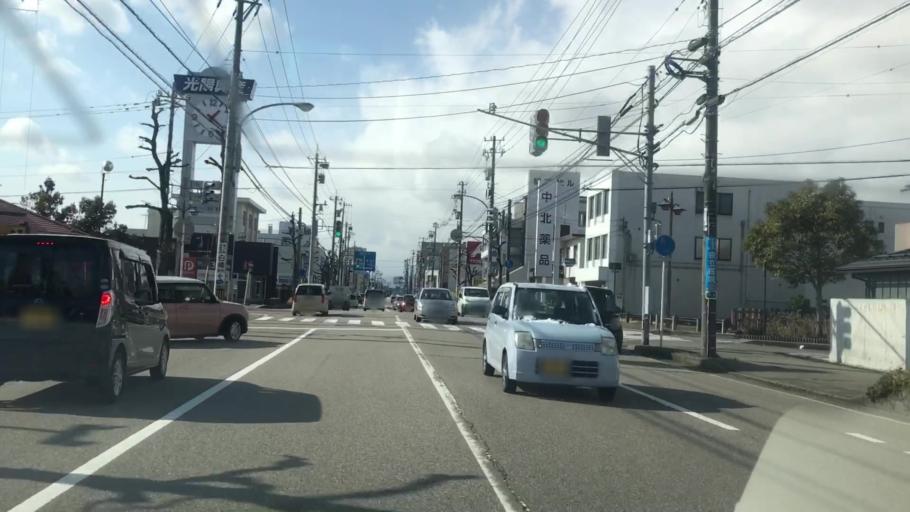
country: JP
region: Toyama
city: Takaoka
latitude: 36.7387
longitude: 137.0183
